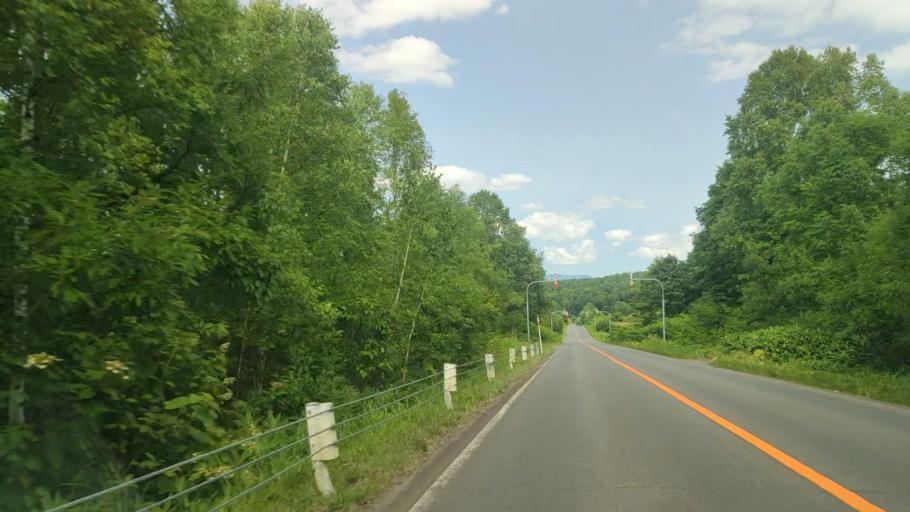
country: JP
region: Hokkaido
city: Nayoro
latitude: 44.2506
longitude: 142.4177
